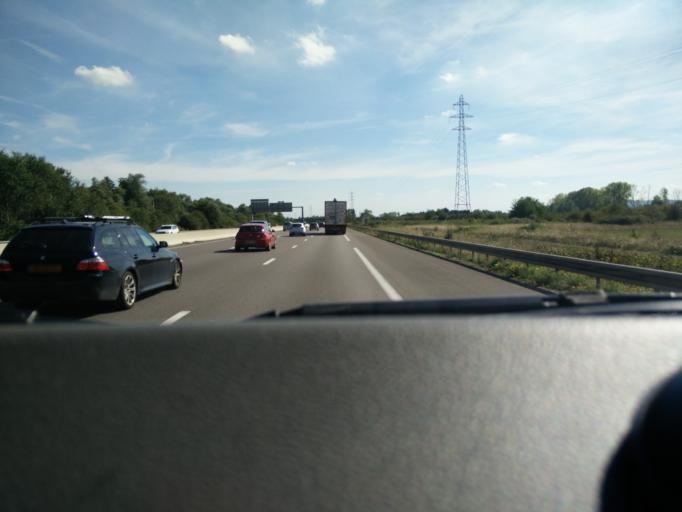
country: FR
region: Lorraine
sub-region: Departement de la Moselle
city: Maizieres-les-Metz
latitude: 49.1892
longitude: 6.1760
